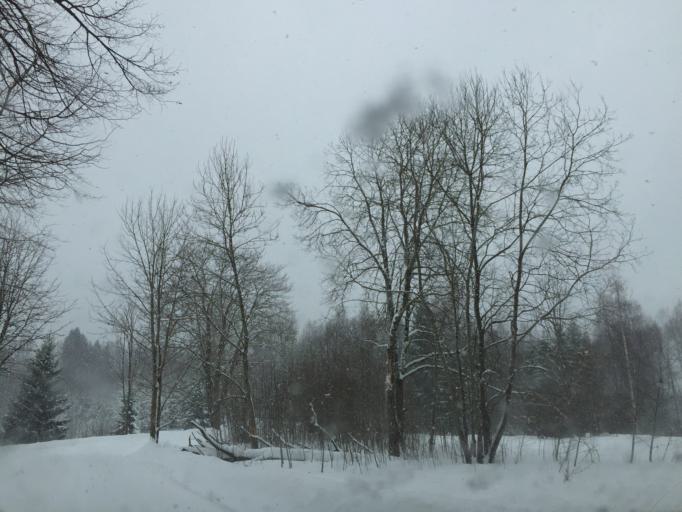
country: LV
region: Amatas Novads
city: Drabesi
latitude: 57.0832
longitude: 25.3904
